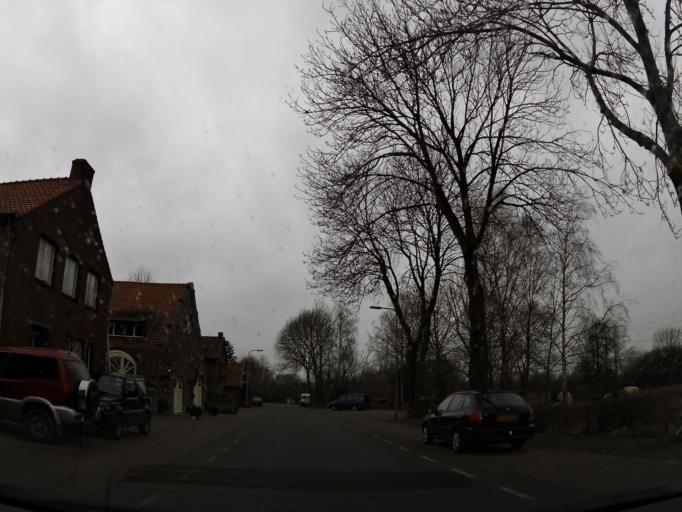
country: BE
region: Flanders
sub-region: Provincie Limburg
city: Maaseik
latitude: 51.1207
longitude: 5.8237
